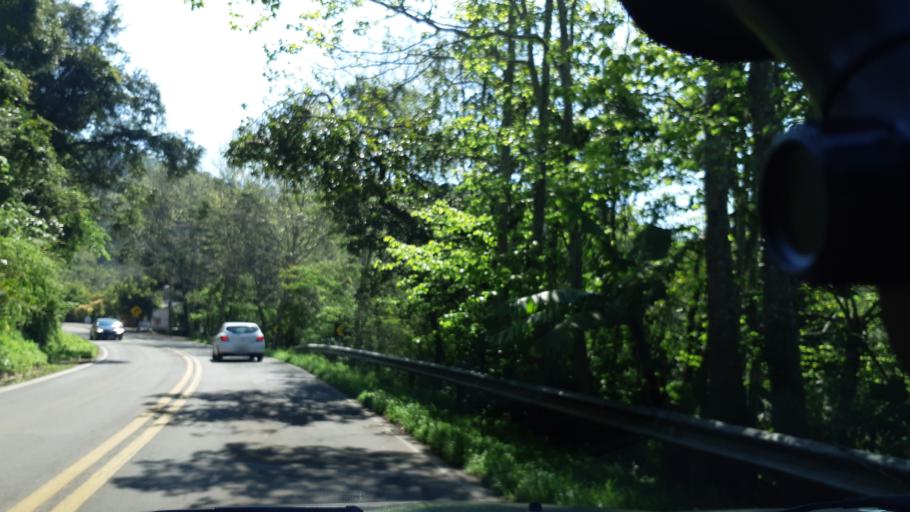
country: BR
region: Rio Grande do Sul
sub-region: Nova Petropolis
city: Nova Petropolis
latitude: -29.4070
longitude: -51.1295
